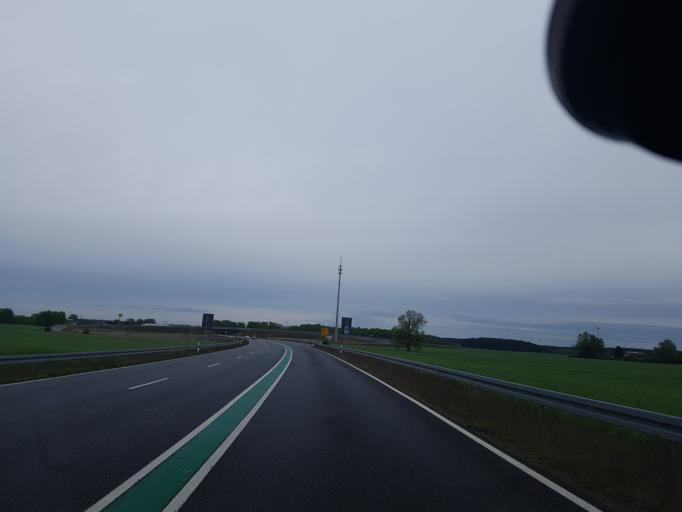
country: DE
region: Brandenburg
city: Drebkau
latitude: 51.6410
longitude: 14.2343
